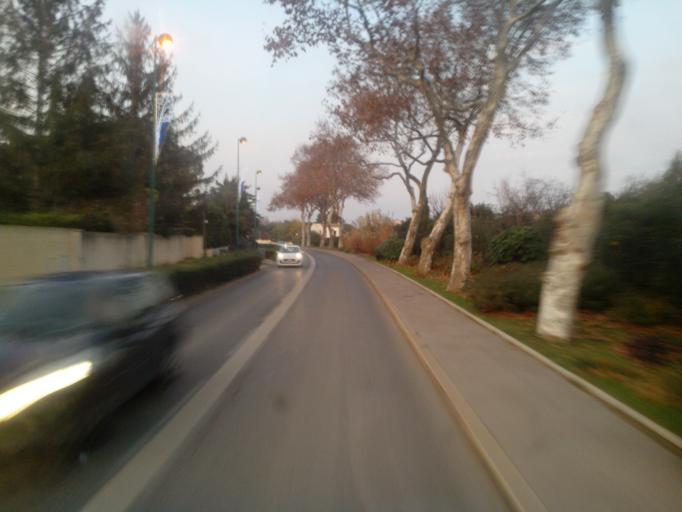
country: FR
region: Languedoc-Roussillon
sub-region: Departement de l'Herault
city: Saint-Just
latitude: 43.6600
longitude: 4.1170
